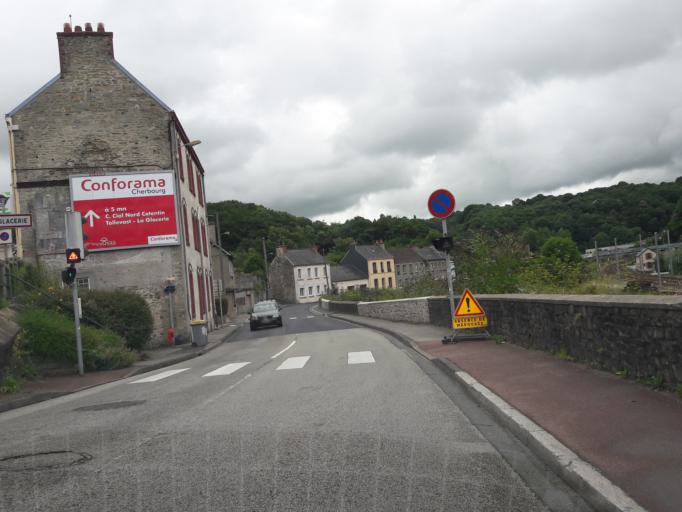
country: FR
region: Lower Normandy
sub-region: Departement de la Manche
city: Cherbourg-Octeville
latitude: 49.6255
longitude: -1.6170
